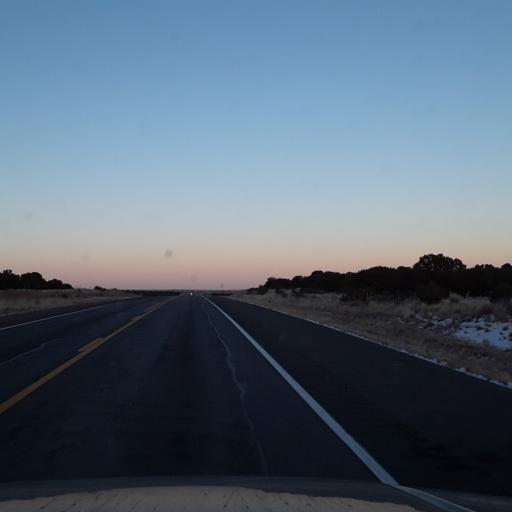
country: US
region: New Mexico
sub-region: Torrance County
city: Estancia
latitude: 34.5200
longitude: -105.3331
